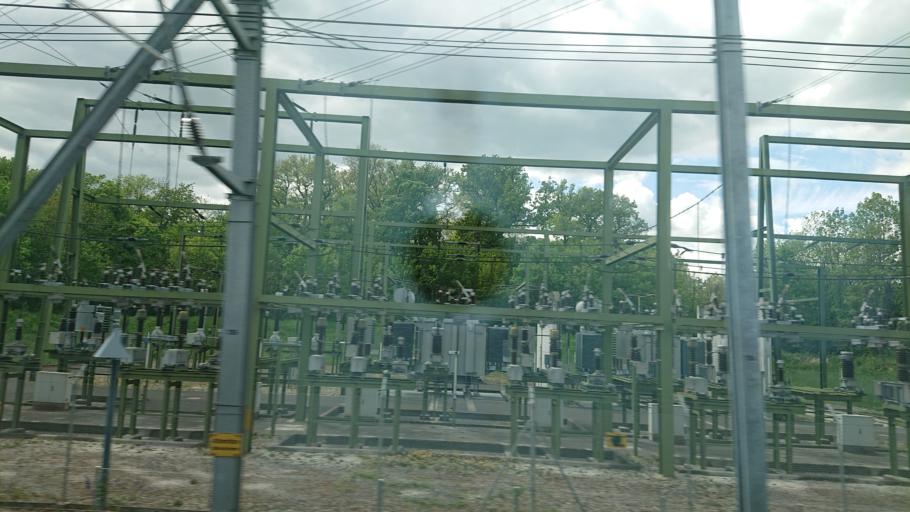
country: CH
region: Geneva
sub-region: Geneva
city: Bellevue
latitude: 46.2497
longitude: 6.1471
